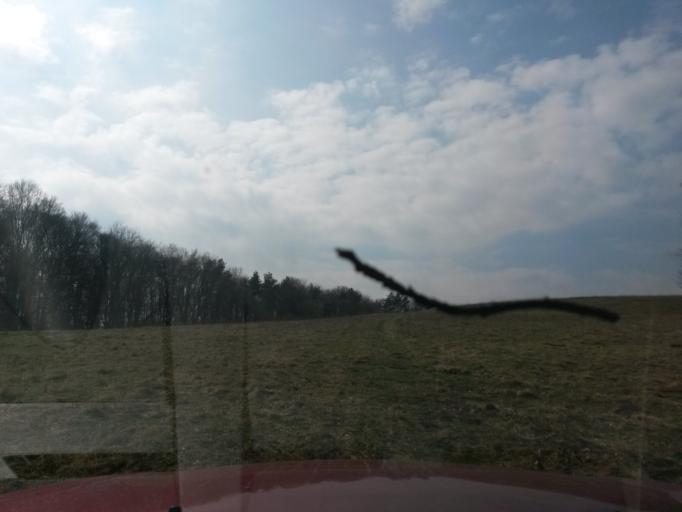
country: SK
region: Presovsky
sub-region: Okres Presov
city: Presov
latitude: 48.9301
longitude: 21.1523
